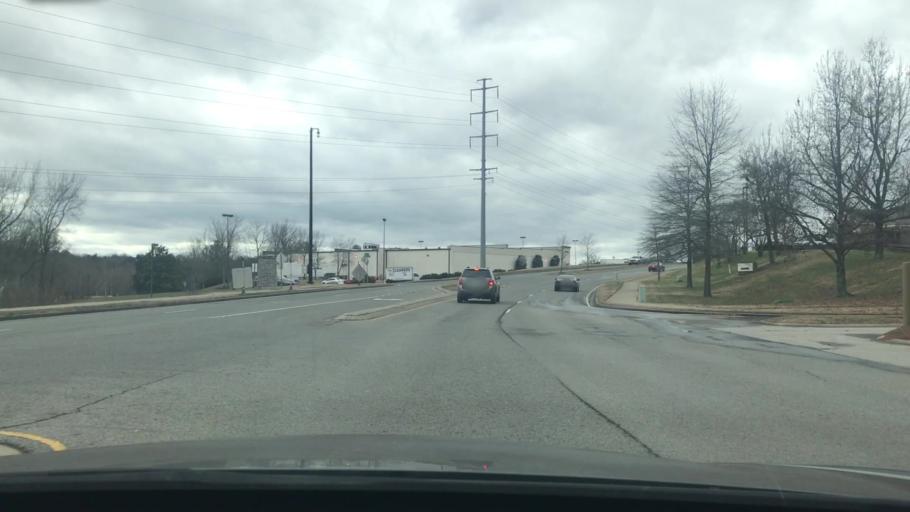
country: US
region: Tennessee
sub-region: Williamson County
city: Franklin
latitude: 35.9158
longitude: -86.8172
